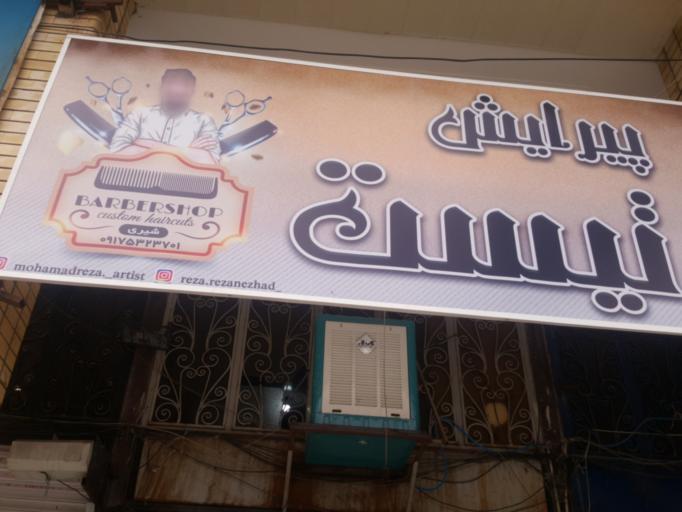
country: IR
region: Fars
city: Marvdasht
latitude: 29.8825
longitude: 52.8108
